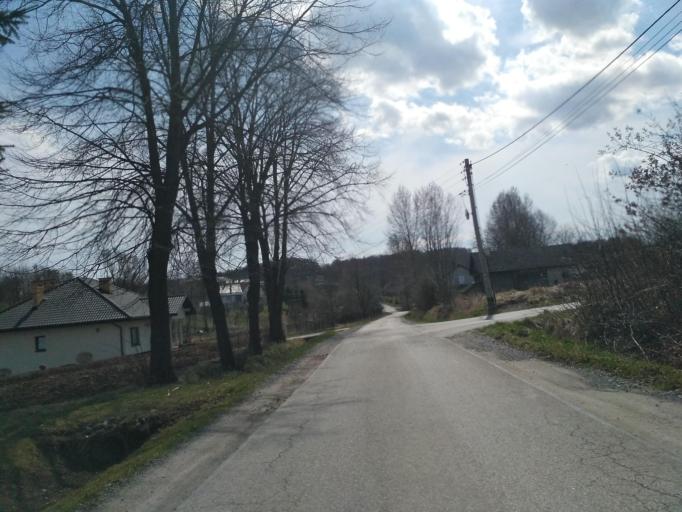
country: PL
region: Subcarpathian Voivodeship
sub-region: Powiat ropczycko-sedziszowski
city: Sedziszow Malopolski
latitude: 50.0479
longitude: 21.7177
